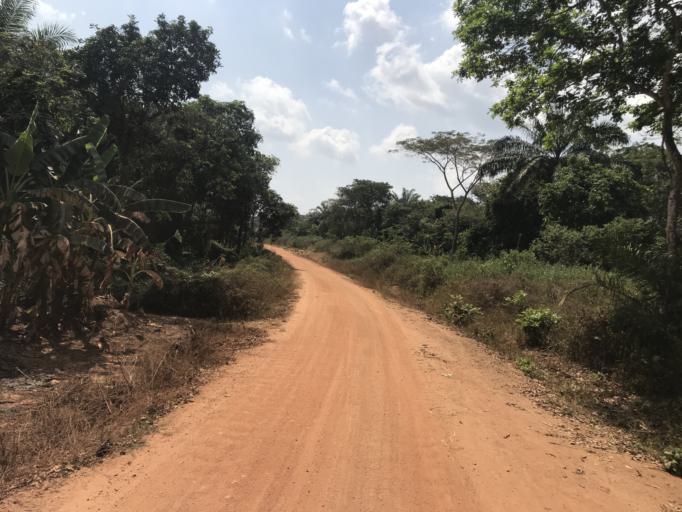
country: NG
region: Osun
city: Ifon
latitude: 7.9657
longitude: 4.5017
